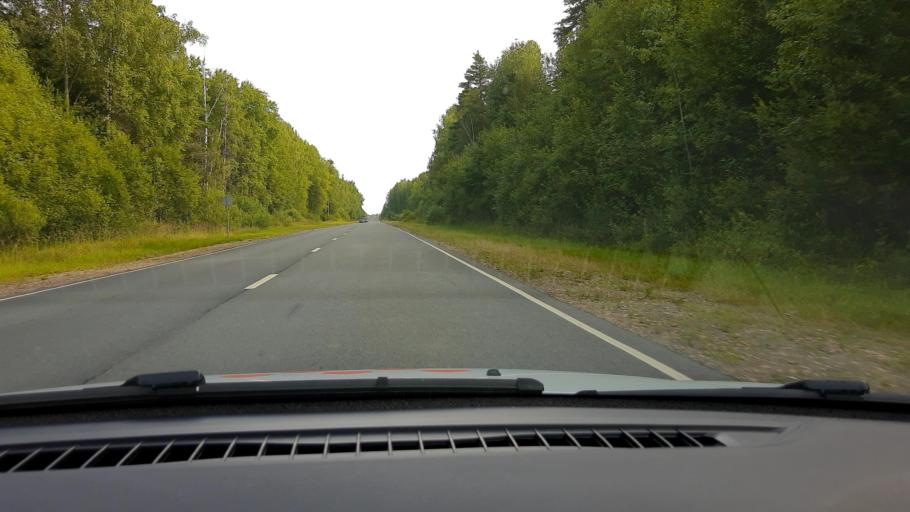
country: RU
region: Nizjnij Novgorod
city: Vladimirskoye
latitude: 56.9402
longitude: 45.0781
